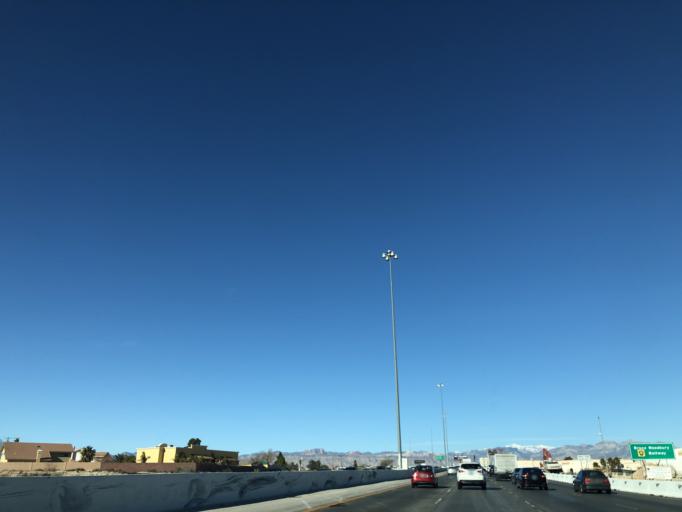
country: US
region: Nevada
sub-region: Clark County
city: Paradise
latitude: 36.0675
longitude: -115.1919
